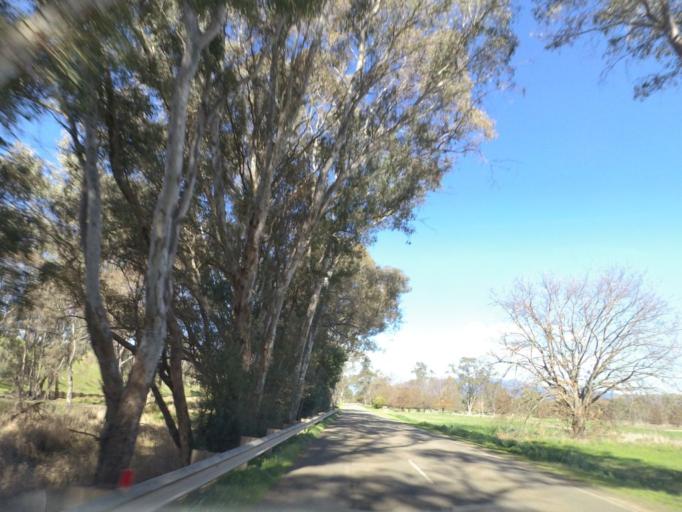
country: AU
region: Victoria
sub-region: Murrindindi
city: Alexandra
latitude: -37.2309
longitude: 145.7656
